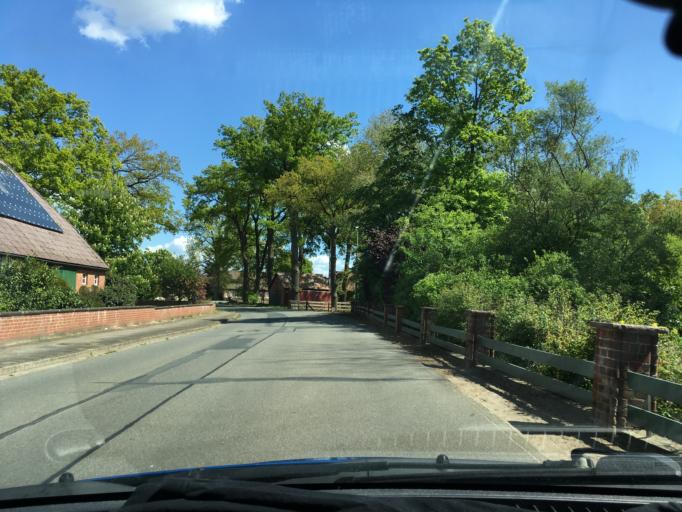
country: DE
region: Lower Saxony
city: Himbergen
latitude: 53.0858
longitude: 10.7418
